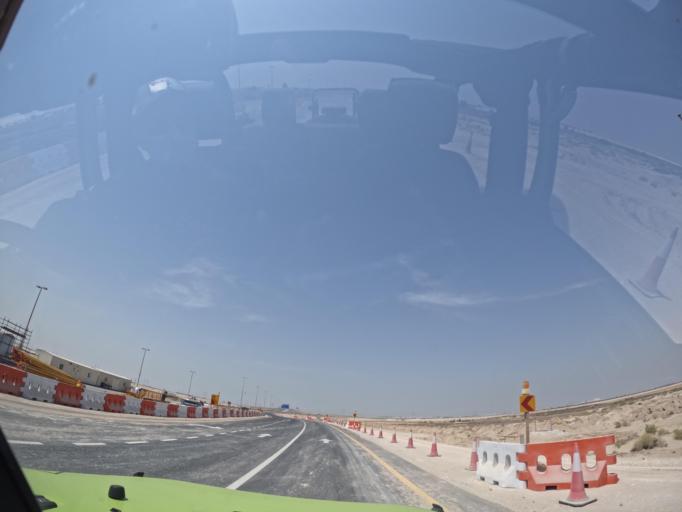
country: AE
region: Abu Dhabi
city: Abu Dhabi
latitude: 24.2398
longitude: 54.4822
